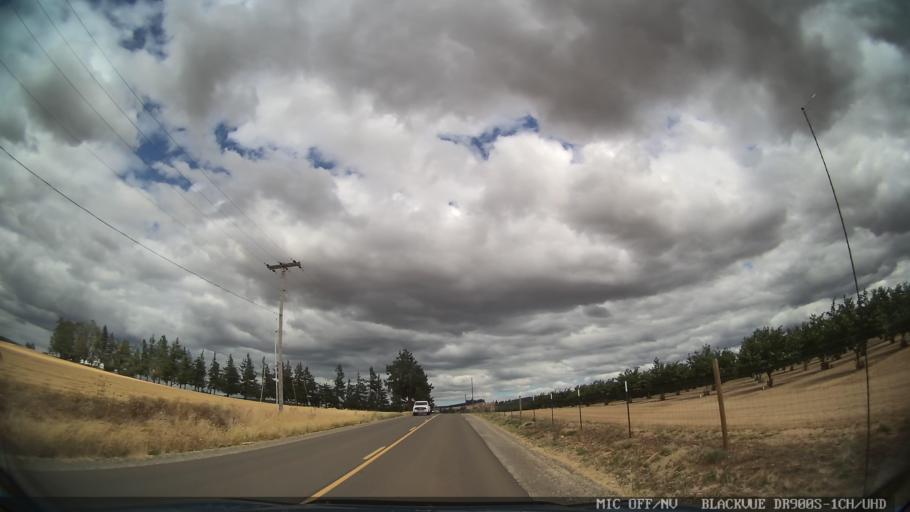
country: US
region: Oregon
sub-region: Marion County
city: Sublimity
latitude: 44.8661
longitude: -122.7674
